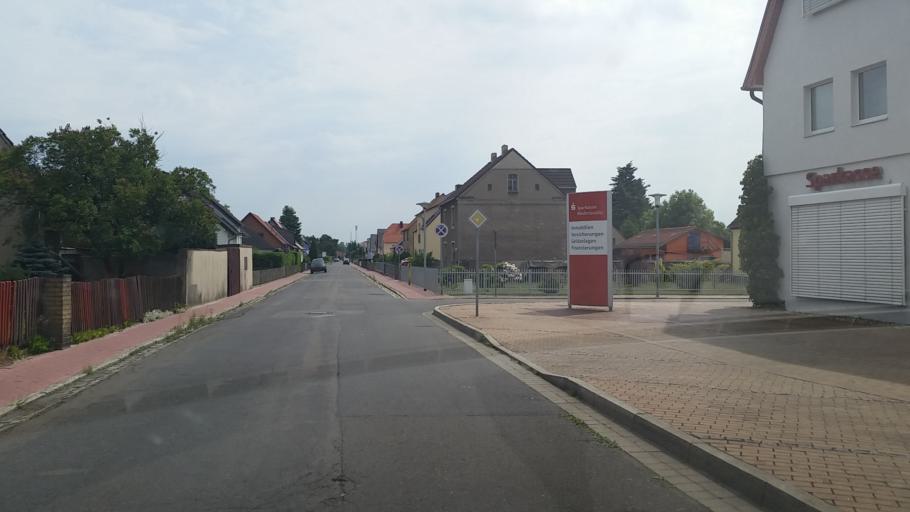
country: DE
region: Brandenburg
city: Schwarzheide
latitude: 51.4793
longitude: 13.8507
